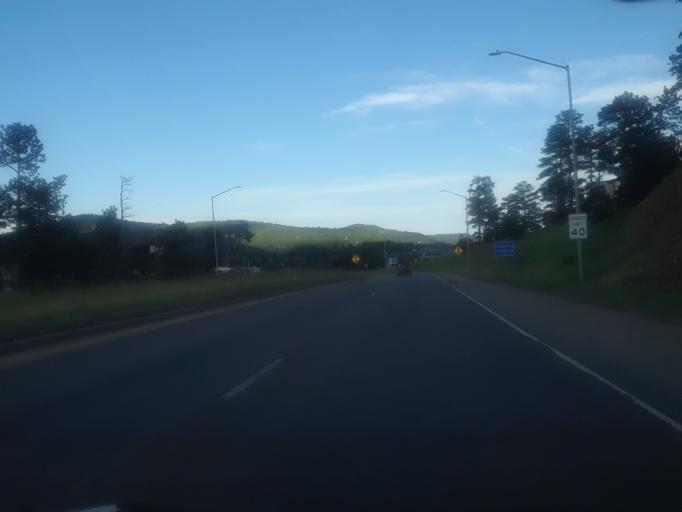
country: US
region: Colorado
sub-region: Jefferson County
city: Kittredge
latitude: 39.6990
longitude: -105.3343
